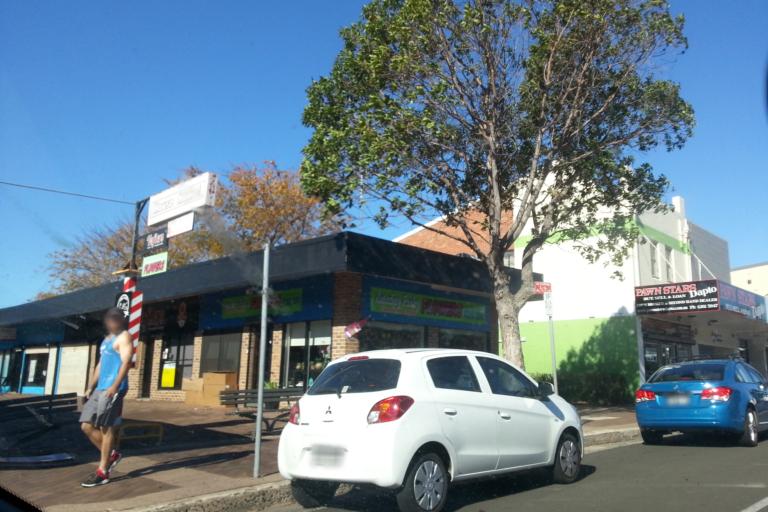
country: AU
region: New South Wales
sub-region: Wollongong
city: Dapto
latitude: -34.4931
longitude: 150.7950
